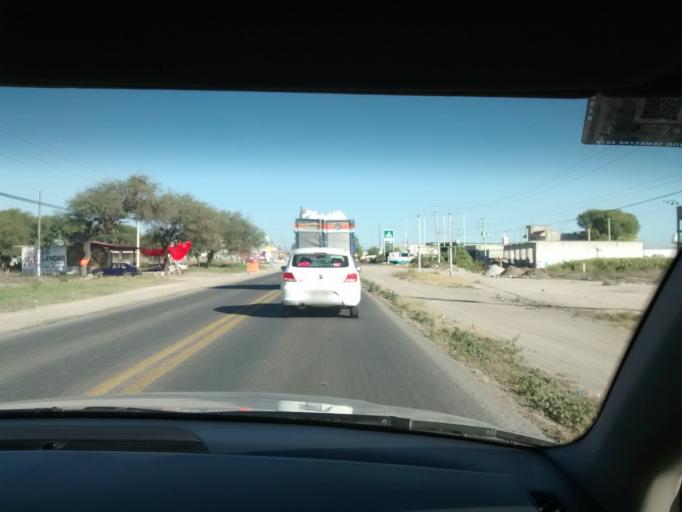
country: MX
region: Puebla
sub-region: Tehuacan
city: Magdalena Cuayucatepec
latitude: 18.5176
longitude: -97.5021
